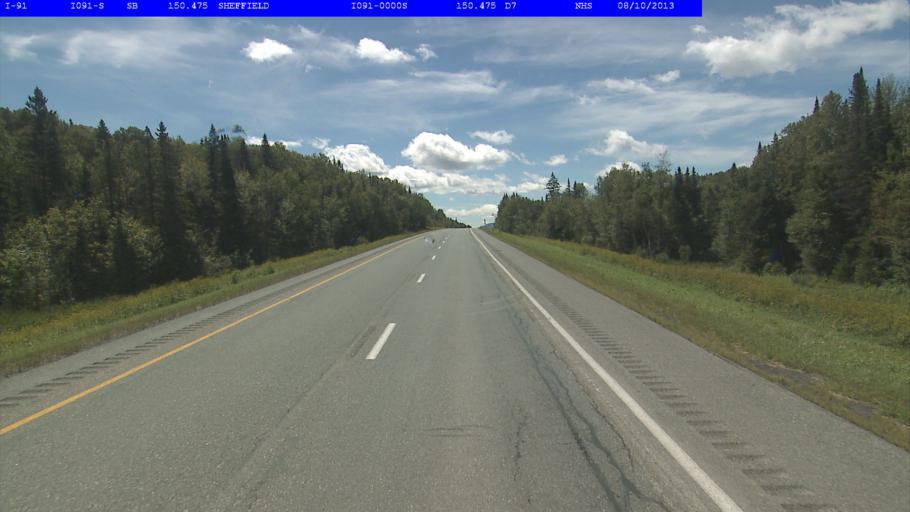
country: US
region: Vermont
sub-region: Caledonia County
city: Lyndonville
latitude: 44.6715
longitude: -72.1330
